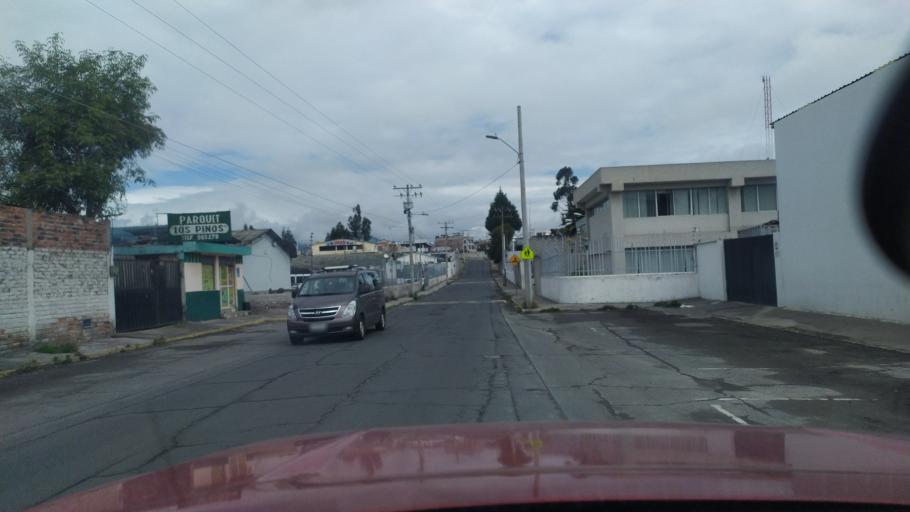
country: EC
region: Chimborazo
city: Riobamba
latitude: -1.6780
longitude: -78.6359
